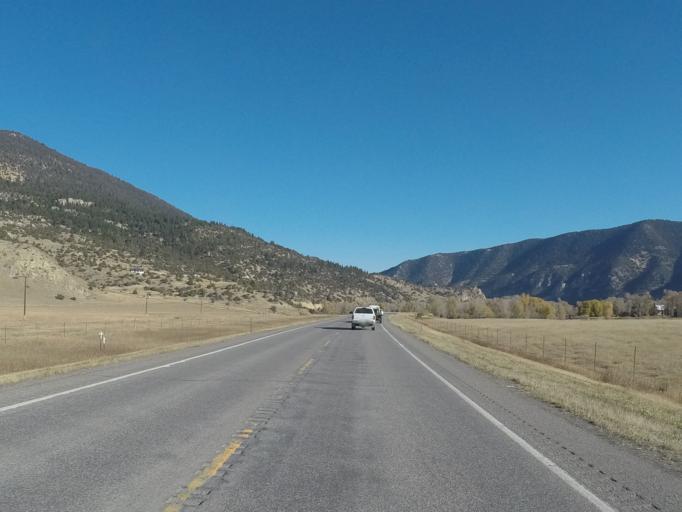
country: US
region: Montana
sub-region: Park County
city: Livingston
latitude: 45.5712
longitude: -110.5889
